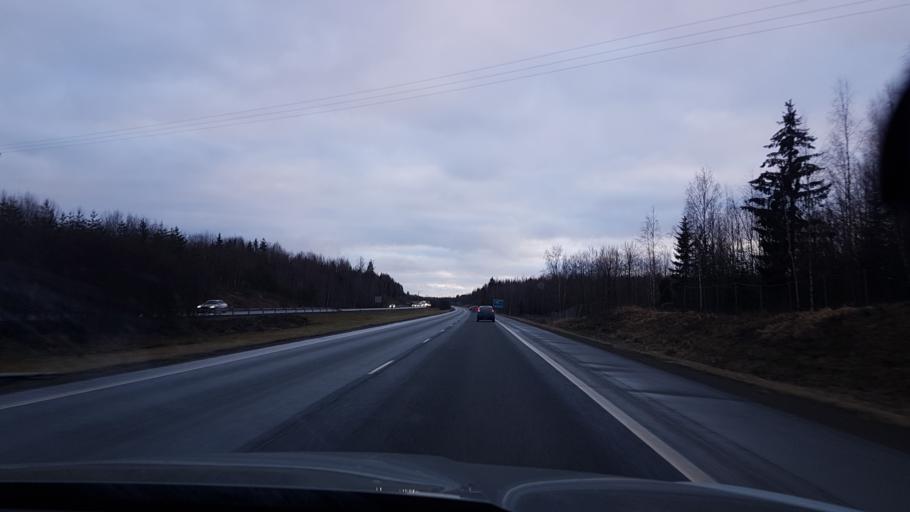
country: FI
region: Pirkanmaa
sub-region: Etelae-Pirkanmaa
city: Toijala
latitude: 61.2359
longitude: 23.8369
